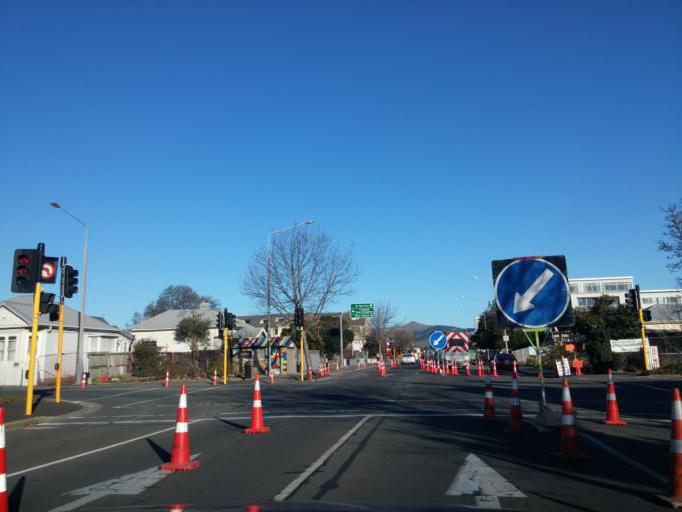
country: NZ
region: Canterbury
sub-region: Christchurch City
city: Christchurch
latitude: -43.5307
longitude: 172.6457
